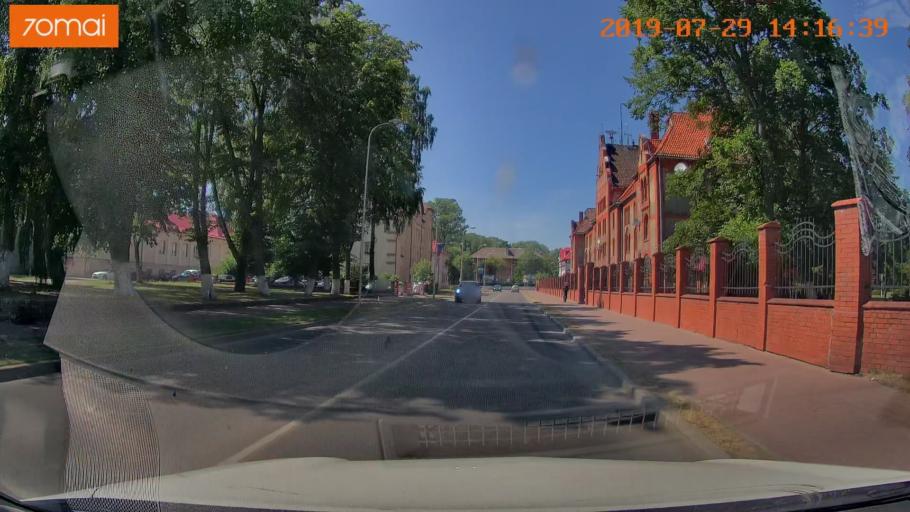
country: RU
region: Kaliningrad
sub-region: Gorod Kaliningrad
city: Baltiysk
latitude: 54.6440
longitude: 19.8945
